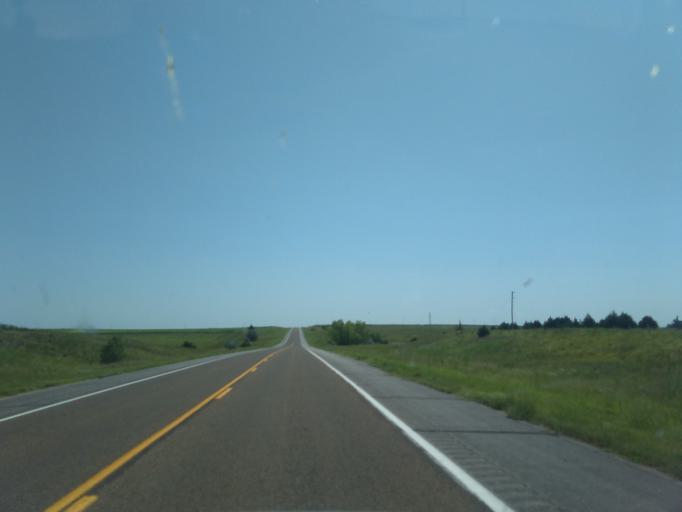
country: US
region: Nebraska
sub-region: Hitchcock County
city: Trenton
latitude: 40.1763
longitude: -101.1260
